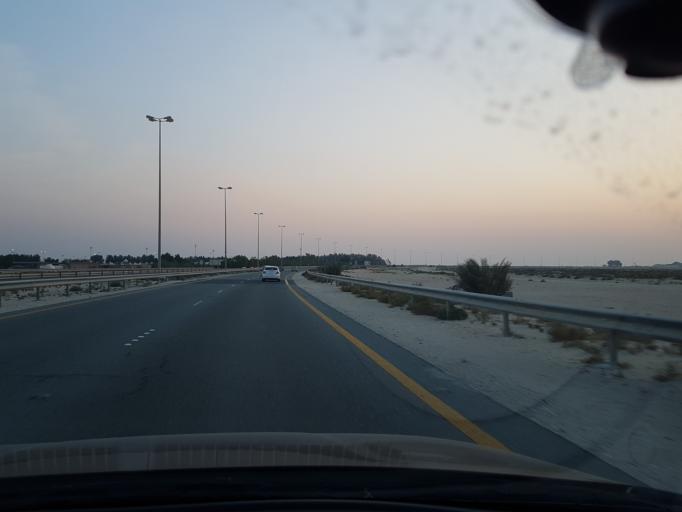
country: BH
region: Central Governorate
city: Dar Kulayb
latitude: 25.9955
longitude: 50.4830
